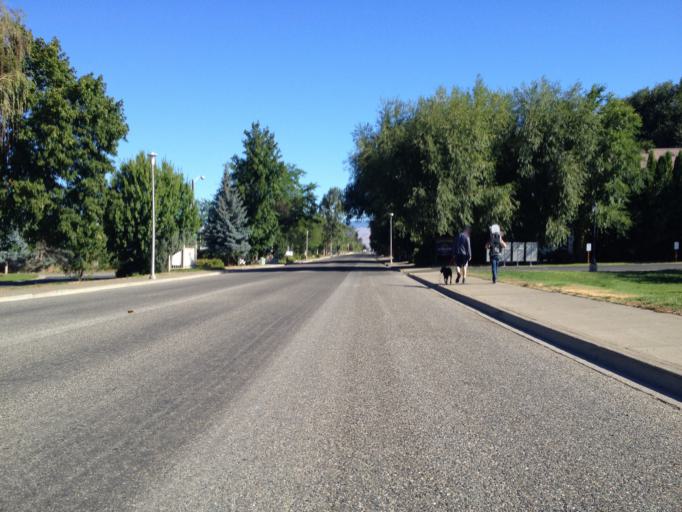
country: US
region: Washington
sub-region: Kittitas County
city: Ellensburg
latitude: 47.0114
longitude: -120.5397
